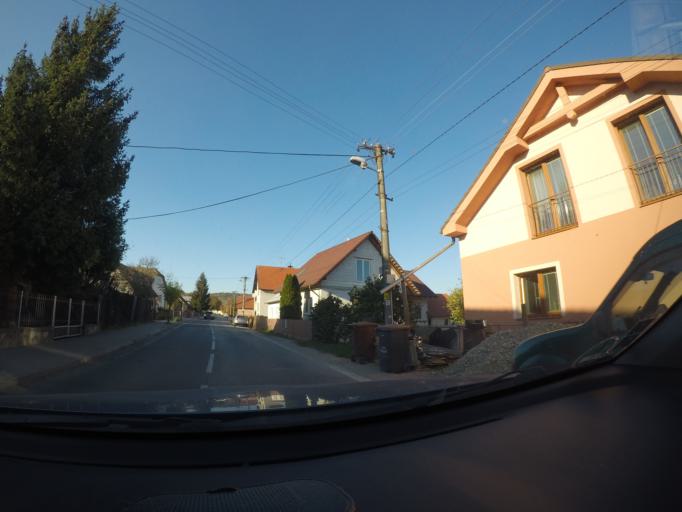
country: SK
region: Nitriansky
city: Nemsova
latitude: 48.9494
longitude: 18.0924
